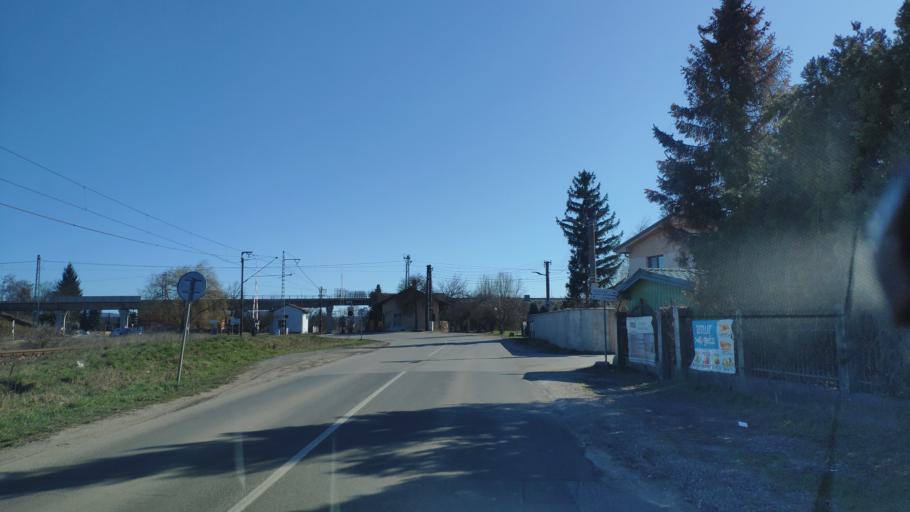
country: SK
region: Kosicky
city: Kosice
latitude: 48.6477
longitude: 21.2871
